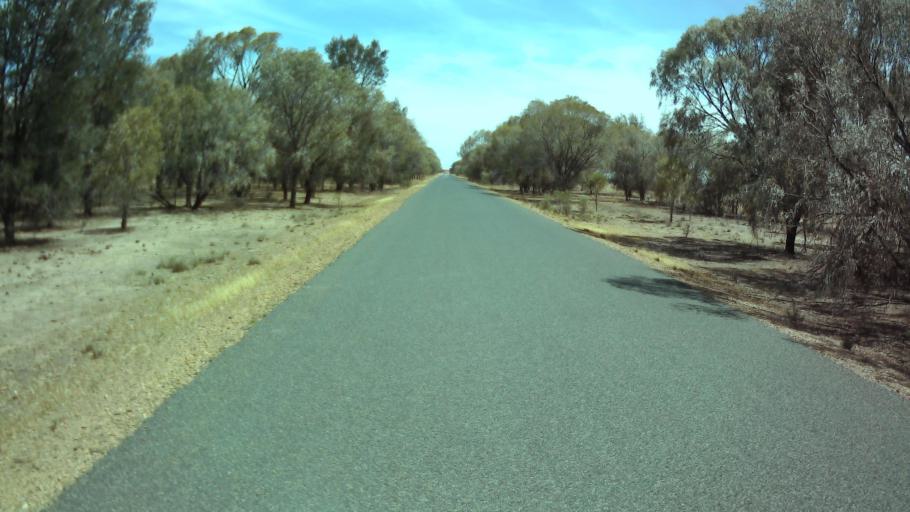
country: AU
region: New South Wales
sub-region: Weddin
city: Grenfell
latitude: -33.8734
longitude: 147.7443
